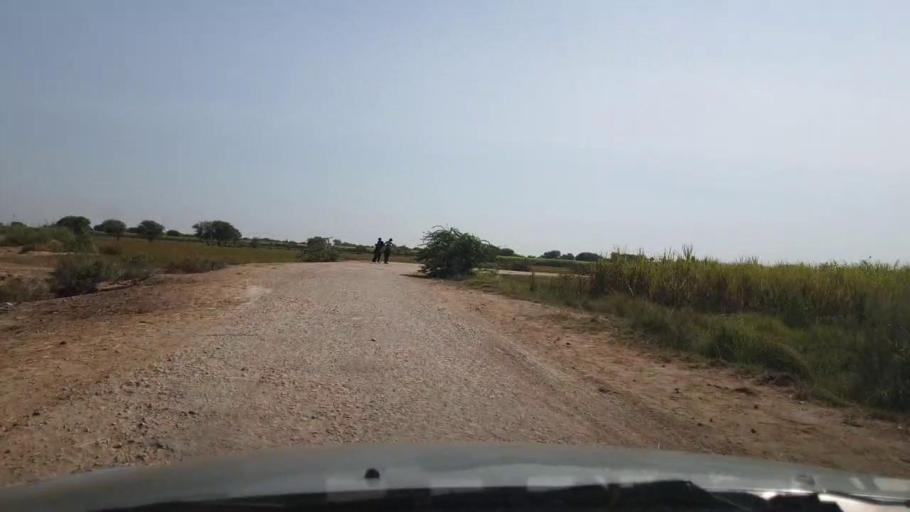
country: PK
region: Sindh
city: Bulri
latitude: 25.0298
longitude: 68.3021
